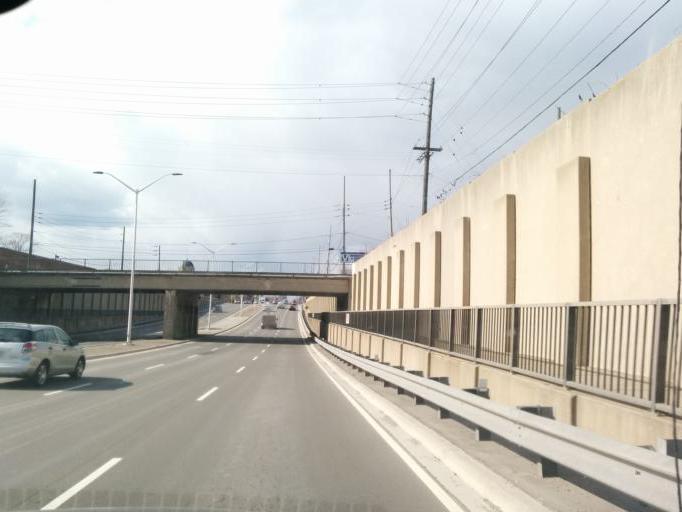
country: CA
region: Ontario
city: Etobicoke
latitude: 43.6059
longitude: -79.5788
